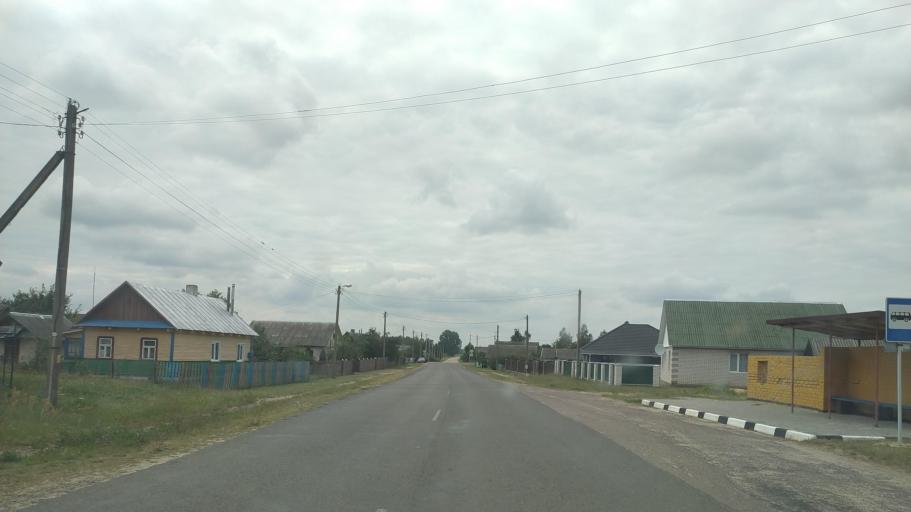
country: BY
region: Brest
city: Byaroza
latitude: 52.5420
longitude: 25.0717
